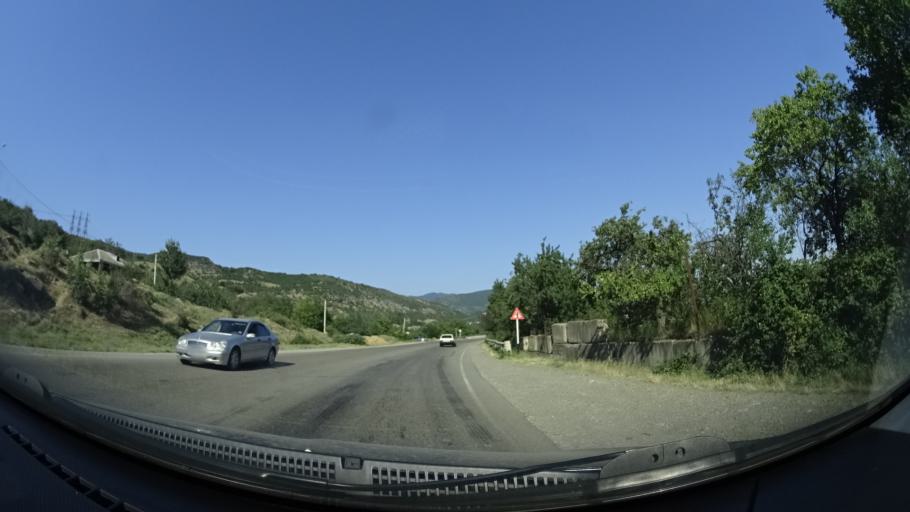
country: GE
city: Zahesi
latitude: 41.8245
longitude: 44.8206
